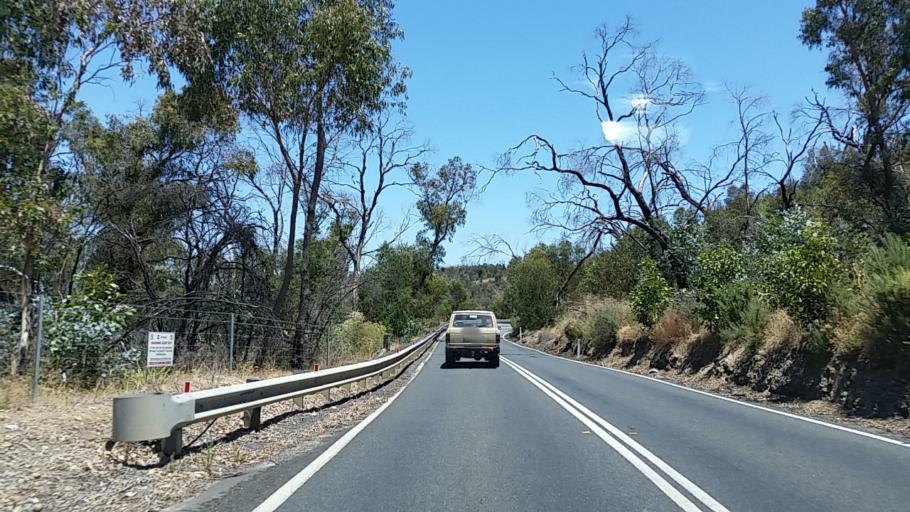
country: AU
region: South Australia
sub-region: Adelaide Hills
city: Gumeracha
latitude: -34.8166
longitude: 138.8077
